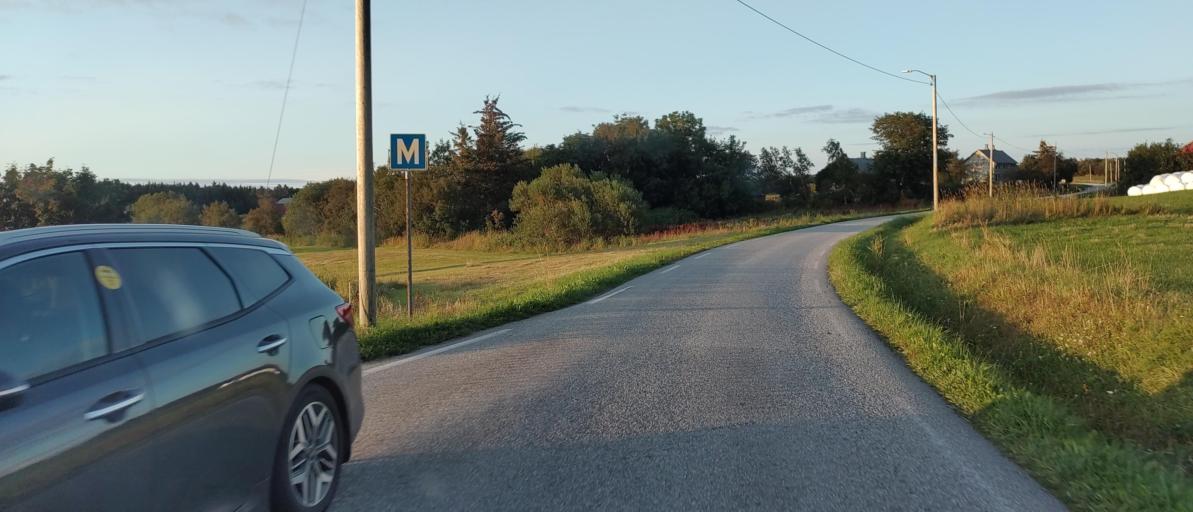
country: NO
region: More og Romsdal
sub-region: Fraena
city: Elnesvagen
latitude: 62.9901
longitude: 7.2119
